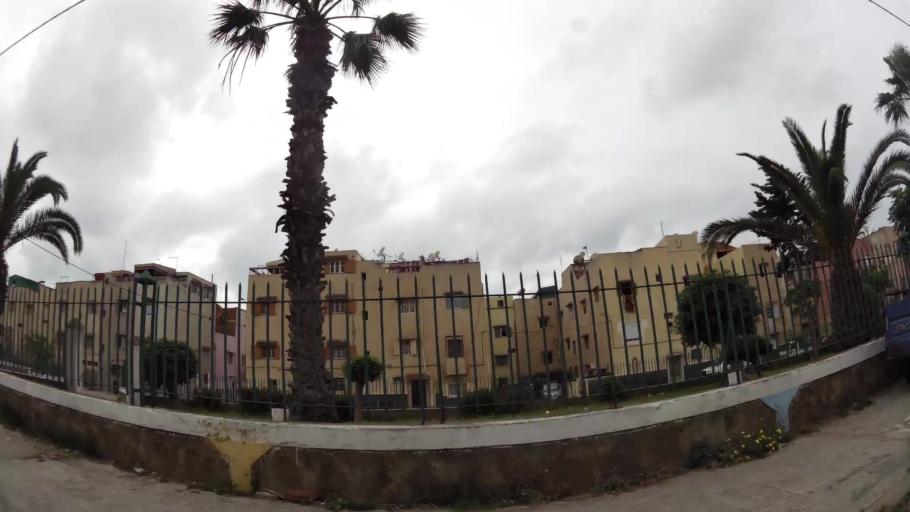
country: MA
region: Rabat-Sale-Zemmour-Zaer
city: Sale
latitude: 34.0449
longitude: -6.8010
